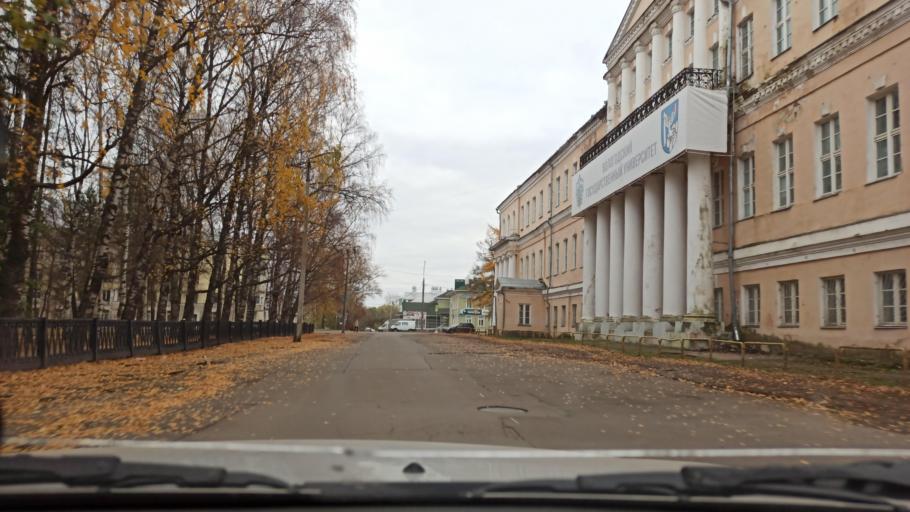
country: RU
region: Vologda
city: Vologda
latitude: 59.2204
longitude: 39.8983
